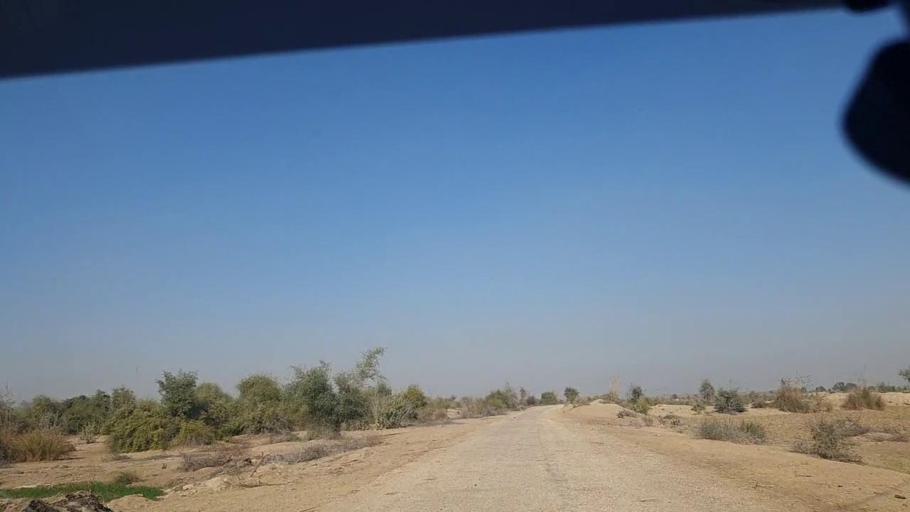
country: PK
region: Sindh
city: Khanpur
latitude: 27.5626
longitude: 69.3369
